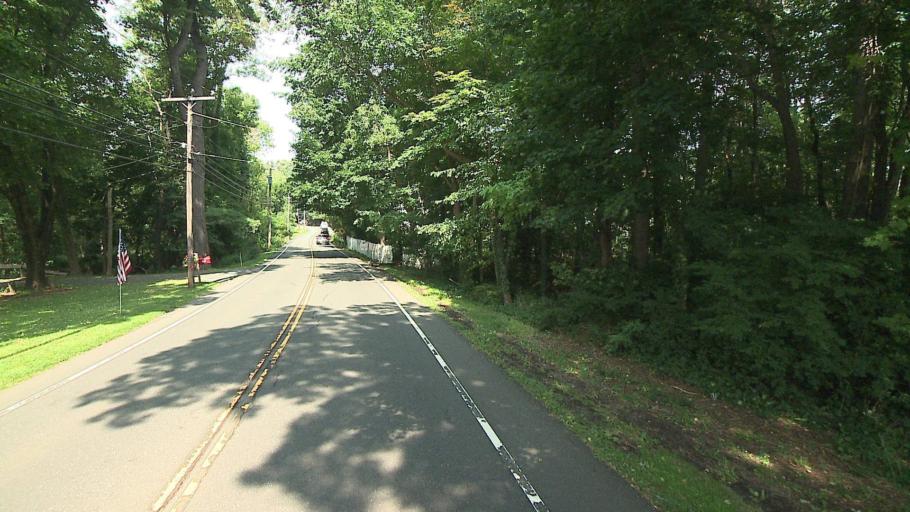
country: US
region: Connecticut
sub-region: Fairfield County
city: Ridgefield
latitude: 41.3100
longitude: -73.5093
